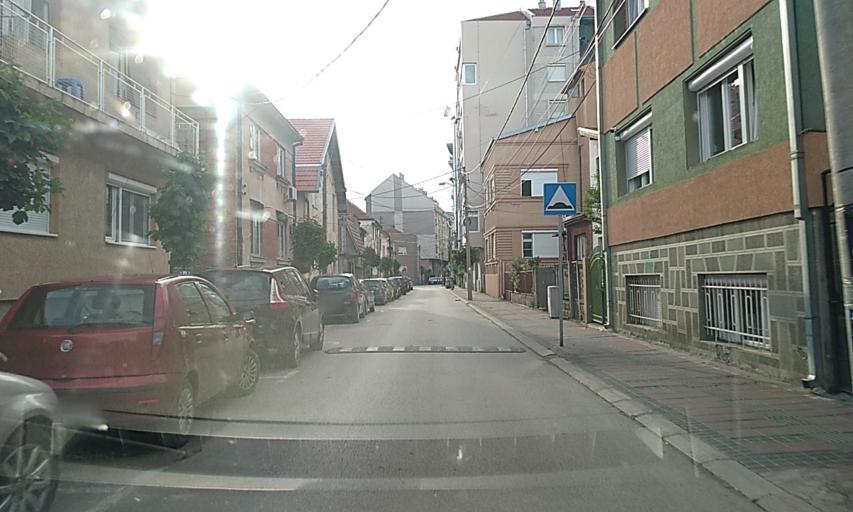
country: RS
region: Central Serbia
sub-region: Nisavski Okrug
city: Nis
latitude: 43.3210
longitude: 21.9057
